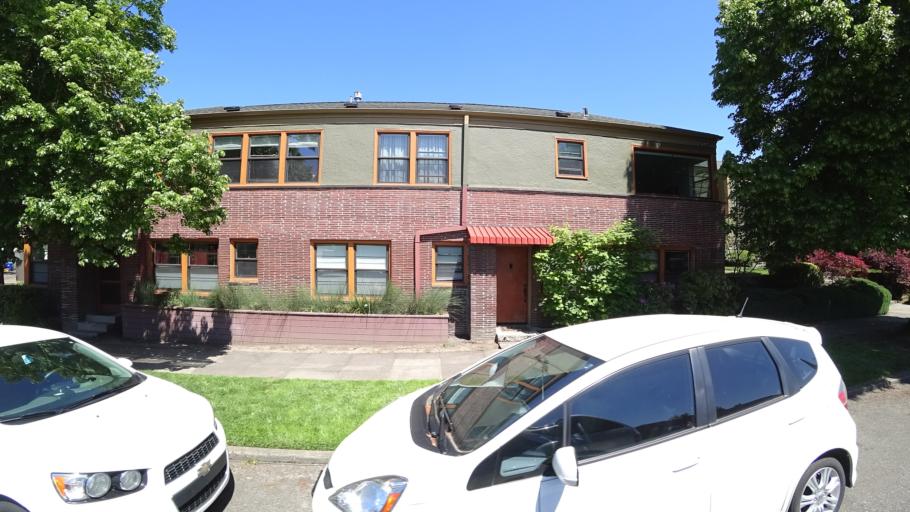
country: US
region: Oregon
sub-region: Multnomah County
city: Portland
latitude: 45.5055
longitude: -122.6448
